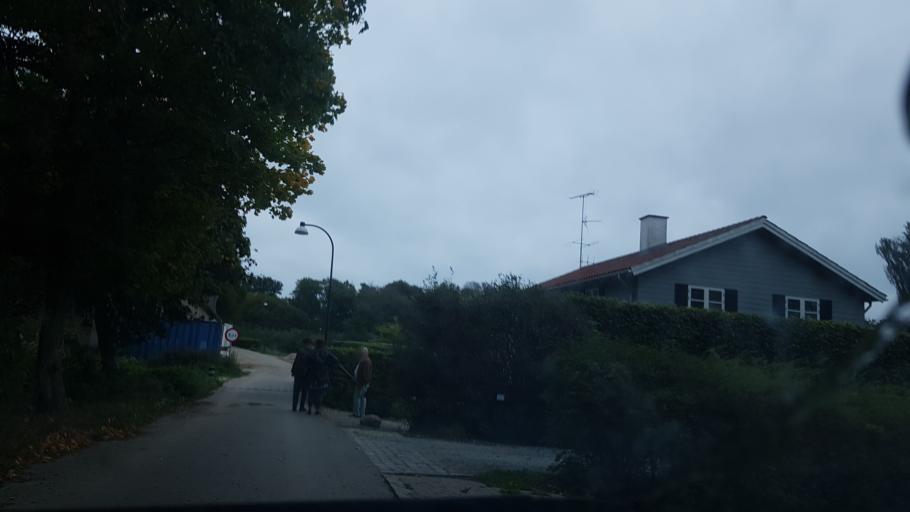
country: DK
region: Capital Region
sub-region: Rudersdal Kommune
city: Trorod
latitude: 55.8419
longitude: 12.5518
